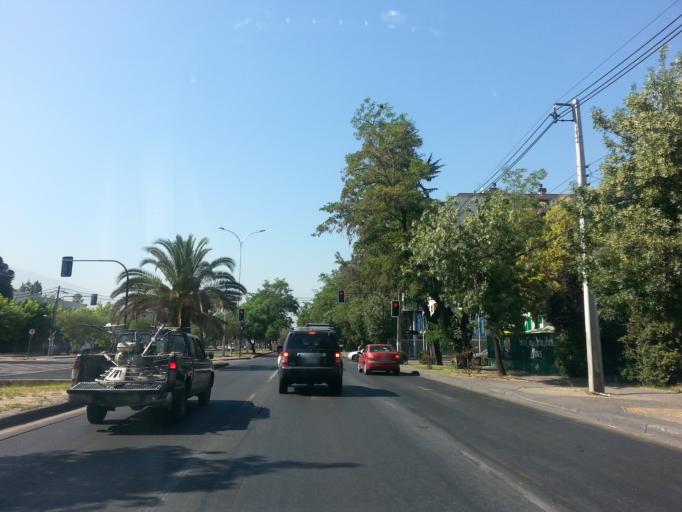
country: CL
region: Santiago Metropolitan
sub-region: Provincia de Santiago
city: Villa Presidente Frei, Nunoa, Santiago, Chile
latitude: -33.4421
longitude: -70.5728
